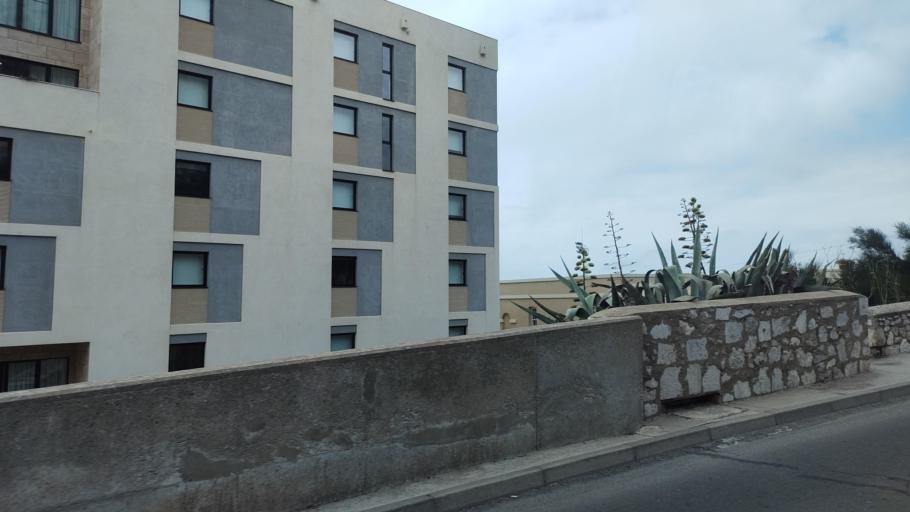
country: GI
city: Gibraltar
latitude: 36.1123
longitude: -5.3462
